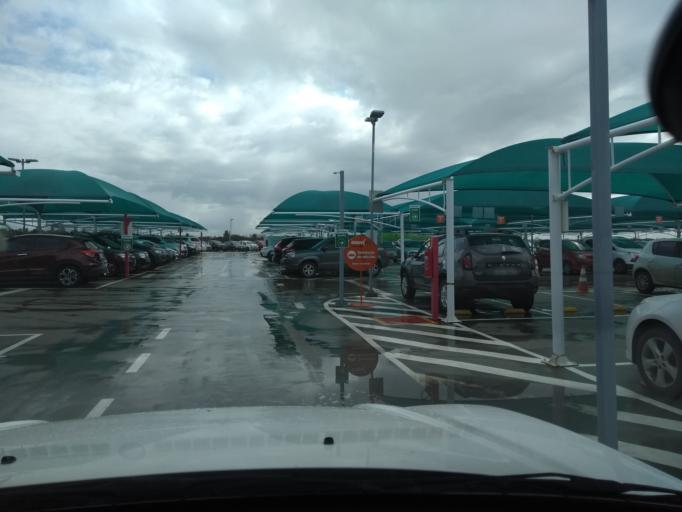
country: BR
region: Bahia
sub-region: Lauro De Freitas
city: Lauro de Freitas
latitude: -12.9138
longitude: -38.3359
